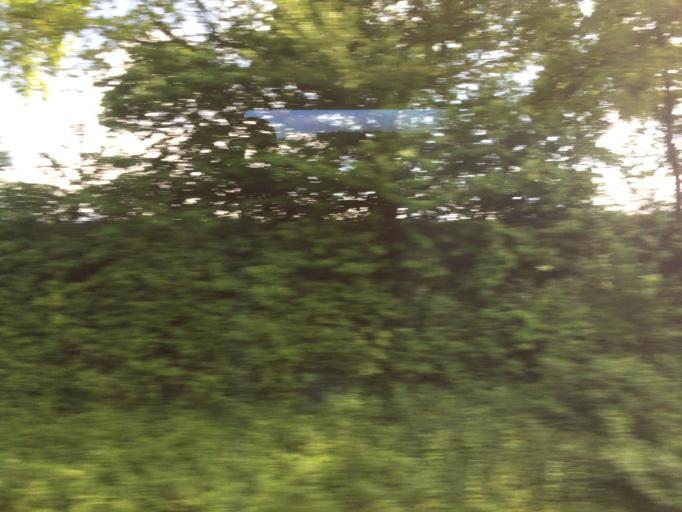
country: DE
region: Bavaria
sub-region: Regierungsbezirk Unterfranken
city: Rottendorf
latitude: 49.8010
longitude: 10.0455
